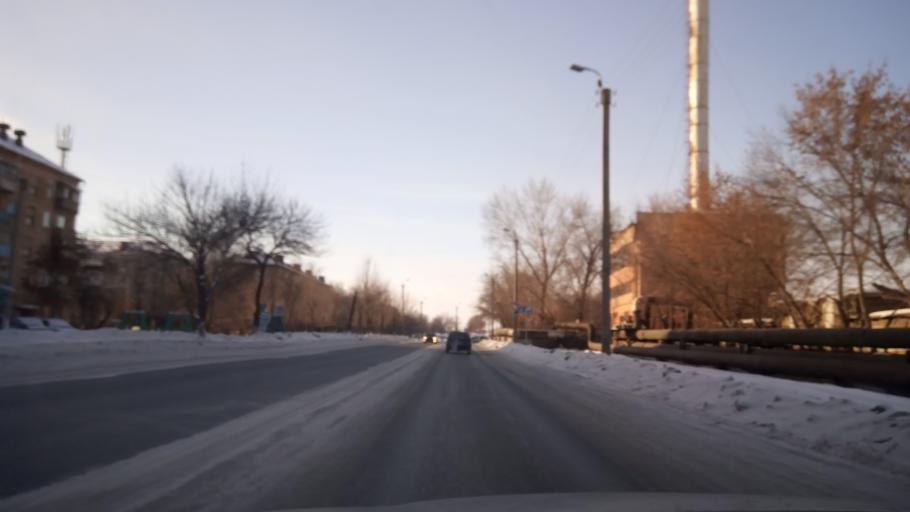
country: RU
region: Orenburg
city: Novotroitsk
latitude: 51.2004
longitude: 58.3094
